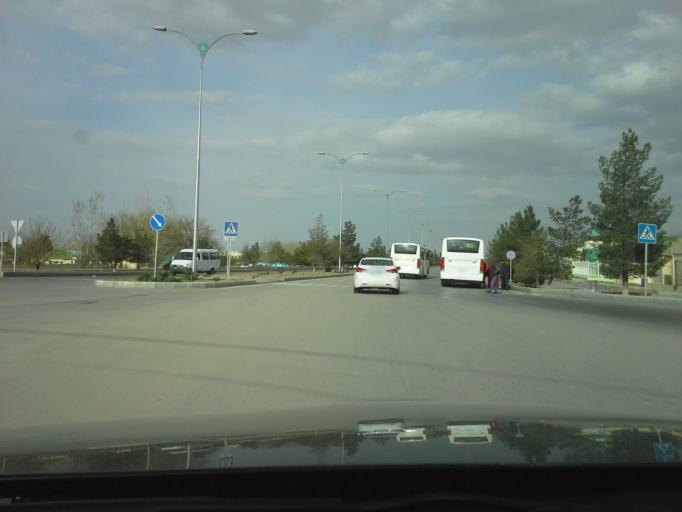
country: TM
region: Ahal
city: Abadan
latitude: 37.9641
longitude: 58.2218
